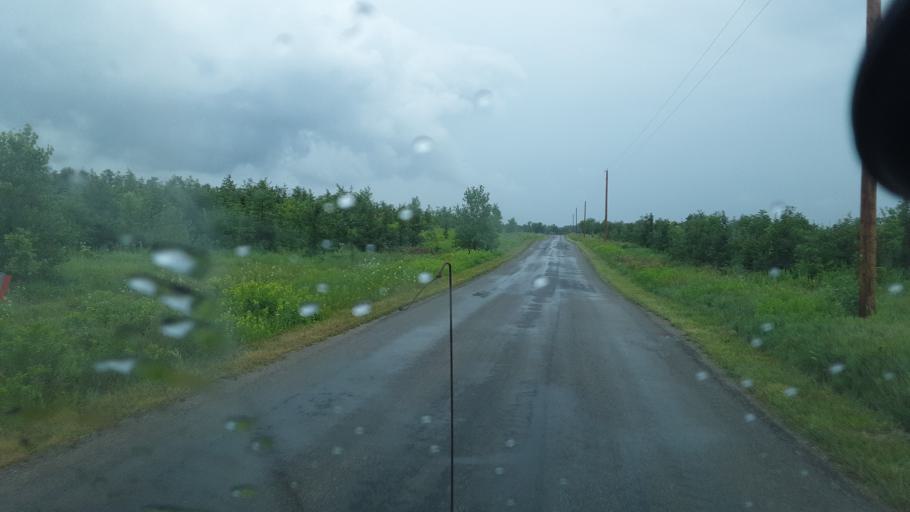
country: US
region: Indiana
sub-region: Steuben County
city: Hamilton
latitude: 41.5490
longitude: -84.8550
